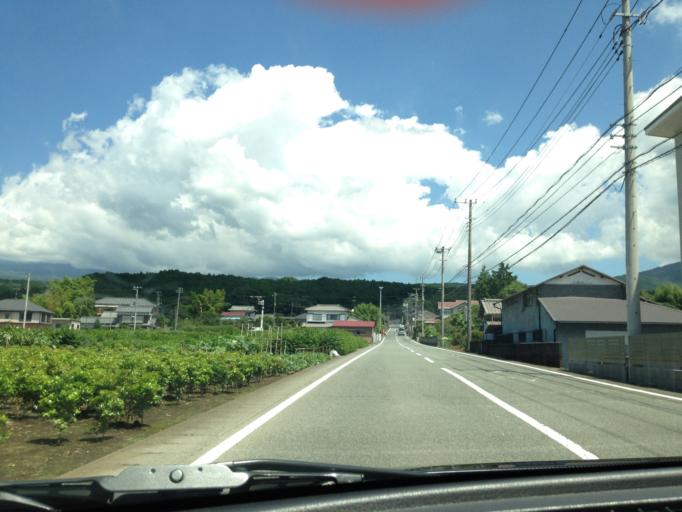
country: JP
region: Shizuoka
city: Fuji
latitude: 35.2035
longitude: 138.7213
